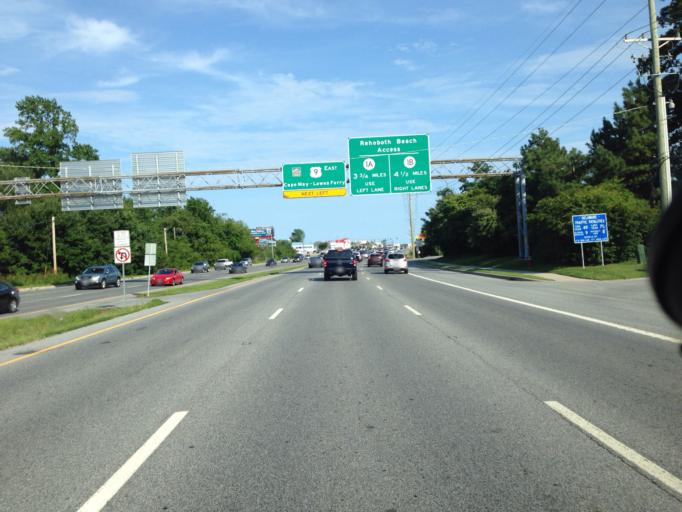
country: US
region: Delaware
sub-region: Sussex County
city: Lewes
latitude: 38.7468
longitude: -75.1569
